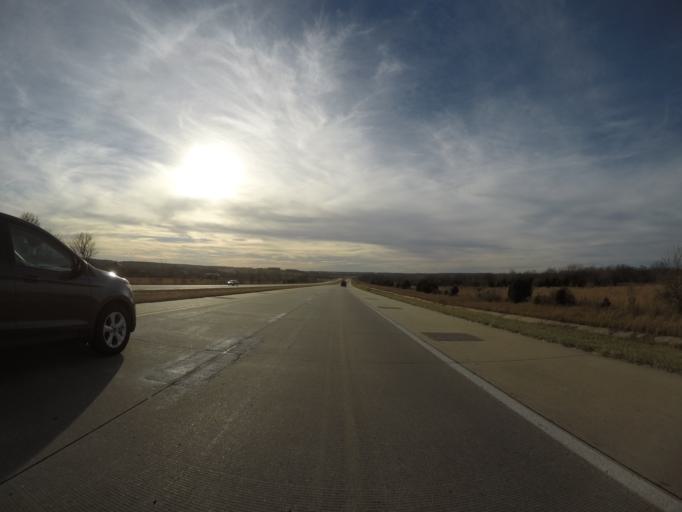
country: US
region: Kansas
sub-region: Franklin County
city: Ottawa
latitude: 38.5619
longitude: -95.3149
